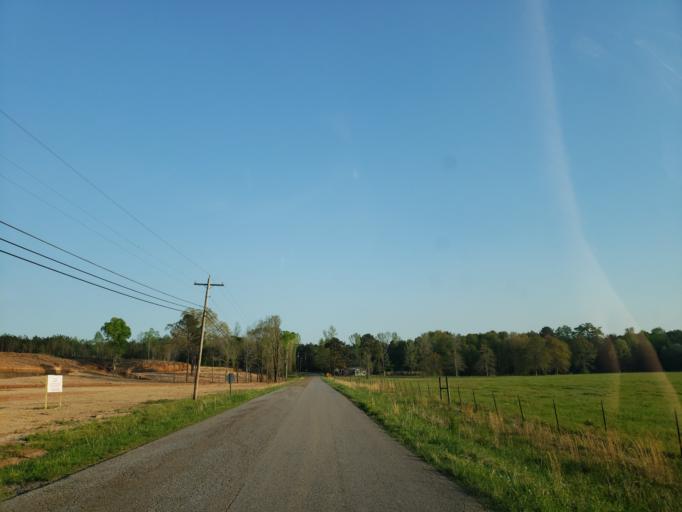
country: US
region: Mississippi
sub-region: Lauderdale County
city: Marion
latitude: 32.4023
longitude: -88.5910
